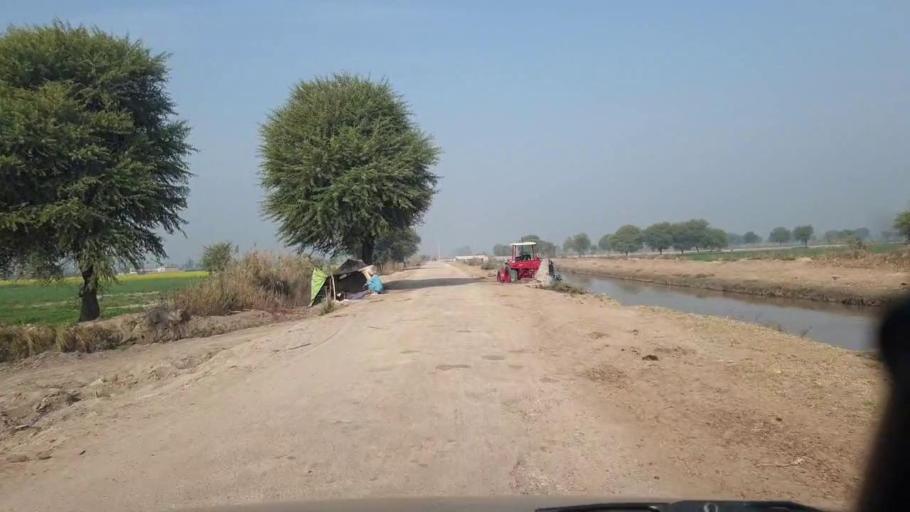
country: PK
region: Sindh
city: Shahdadpur
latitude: 26.0379
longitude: 68.5297
